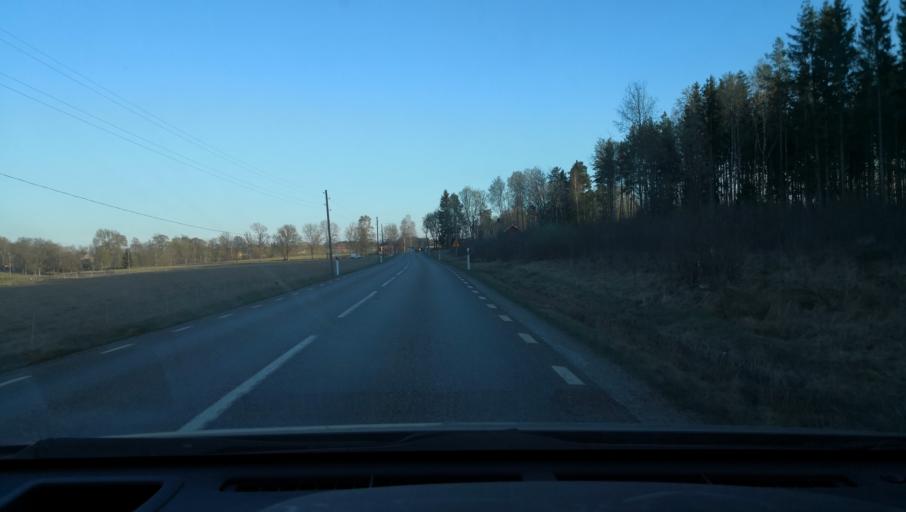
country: SE
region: Uppsala
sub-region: Enkopings Kommun
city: Irsta
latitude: 59.7747
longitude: 16.9105
